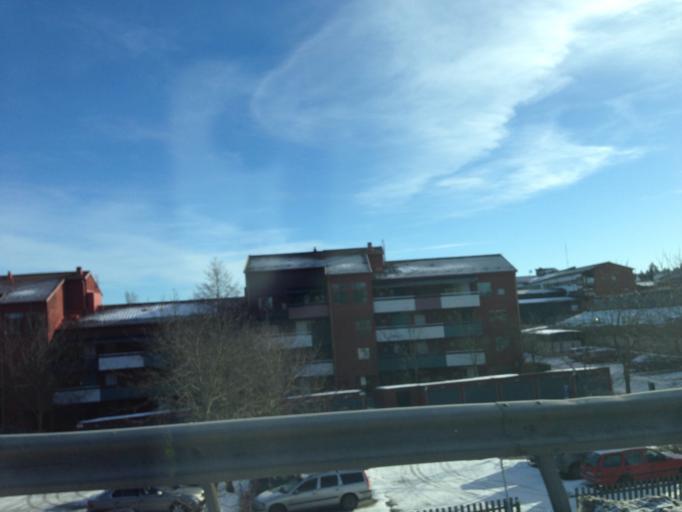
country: SE
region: Stockholm
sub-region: Ekero Kommun
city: Ekeroe
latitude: 59.2924
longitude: 17.8103
